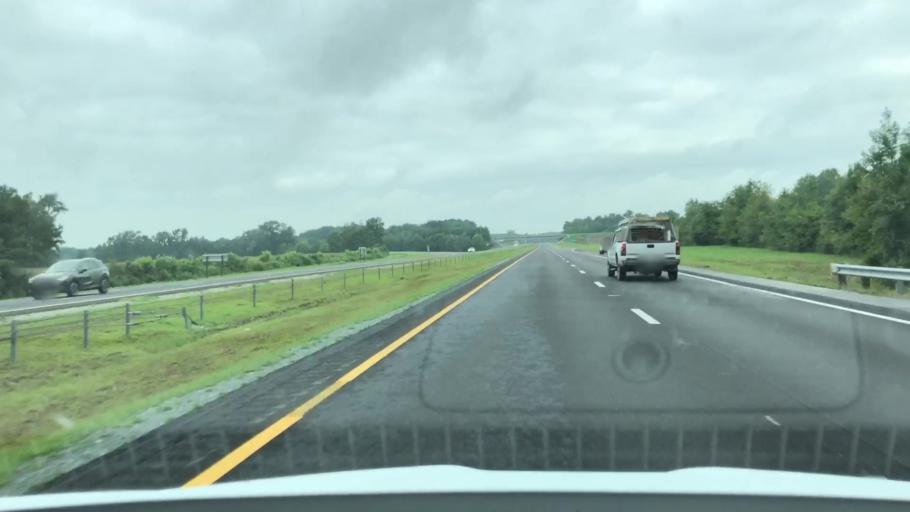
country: US
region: North Carolina
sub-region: Wayne County
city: Fremont
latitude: 35.4898
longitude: -77.9936
